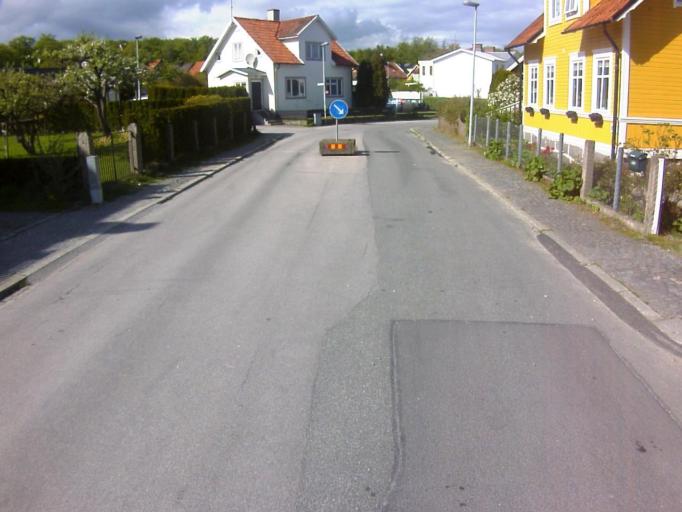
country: SE
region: Blekinge
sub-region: Solvesborgs Kommun
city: Soelvesborg
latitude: 56.0545
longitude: 14.5782
